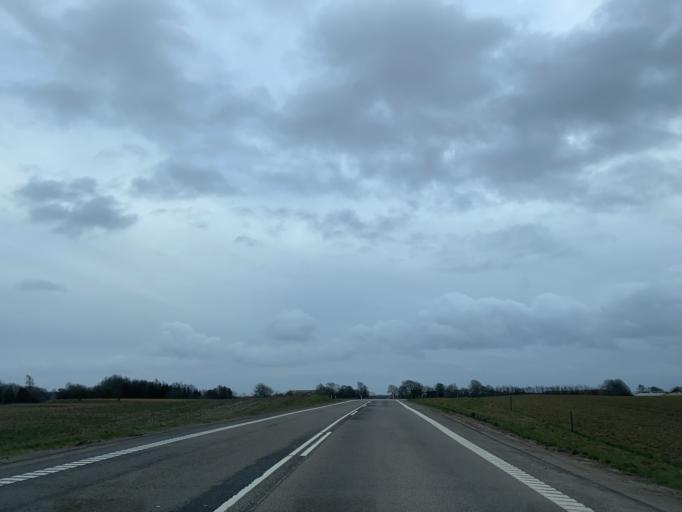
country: DK
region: Central Jutland
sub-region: Viborg Kommune
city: Bjerringbro
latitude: 56.2951
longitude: 9.6017
